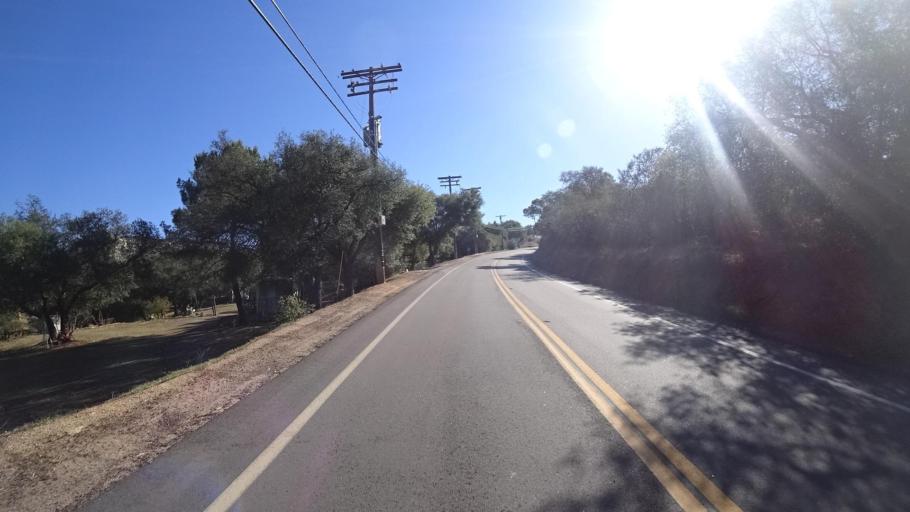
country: US
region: California
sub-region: San Diego County
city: Jamul
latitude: 32.6782
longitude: -116.7477
